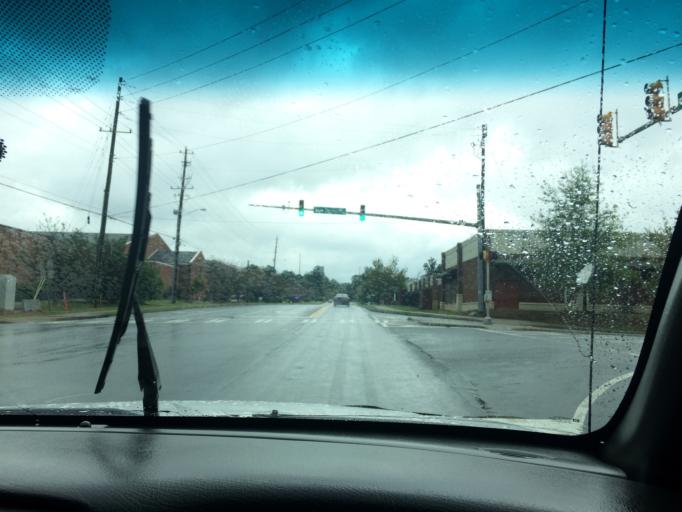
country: US
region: Georgia
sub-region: Cobb County
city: Acworth
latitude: 34.0393
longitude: -84.6513
